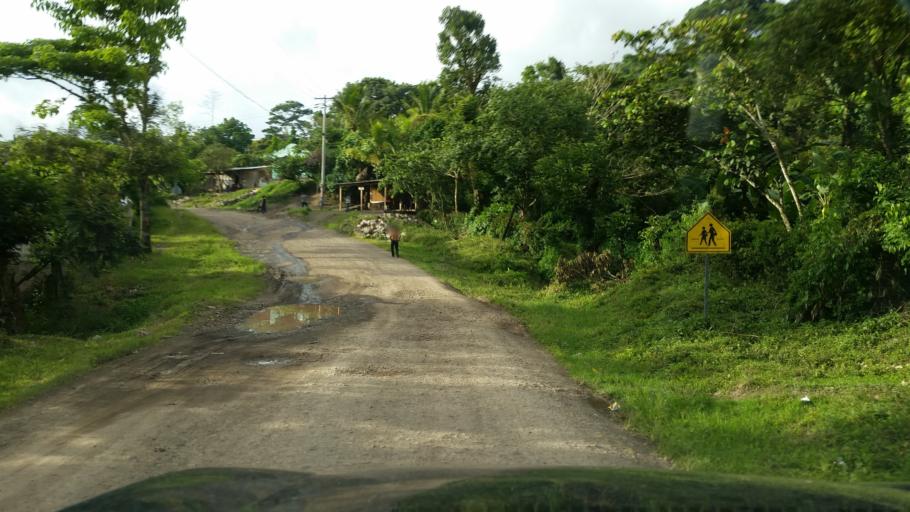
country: NI
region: Jinotega
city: Jinotega
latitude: 13.2332
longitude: -85.7278
